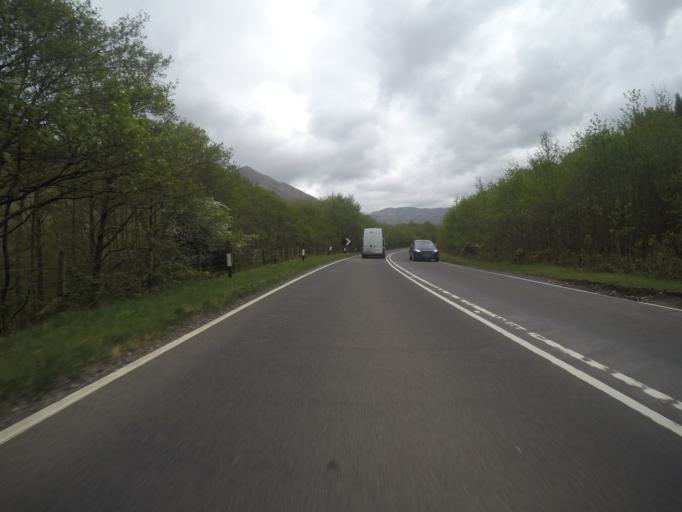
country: GB
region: Scotland
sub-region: Highland
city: Fort William
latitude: 57.2056
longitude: -5.3954
